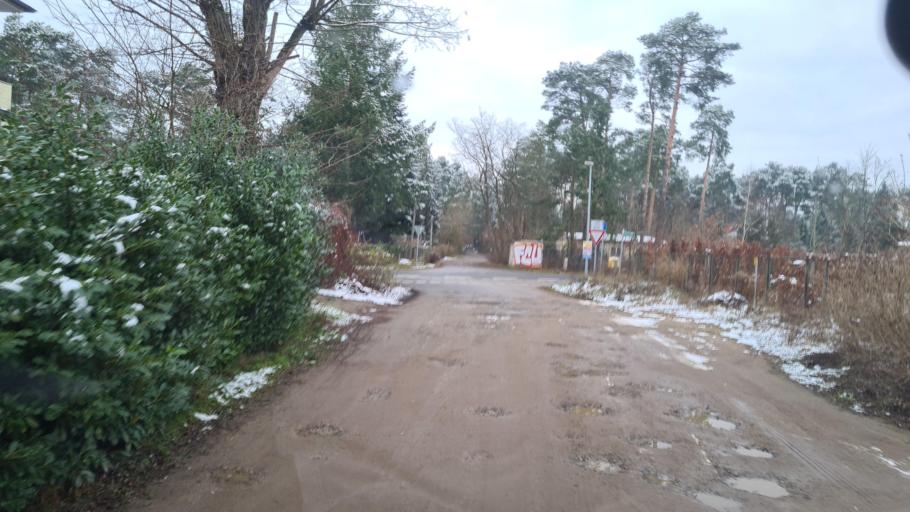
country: DE
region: Brandenburg
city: Grunheide
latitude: 52.4519
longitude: 13.8719
